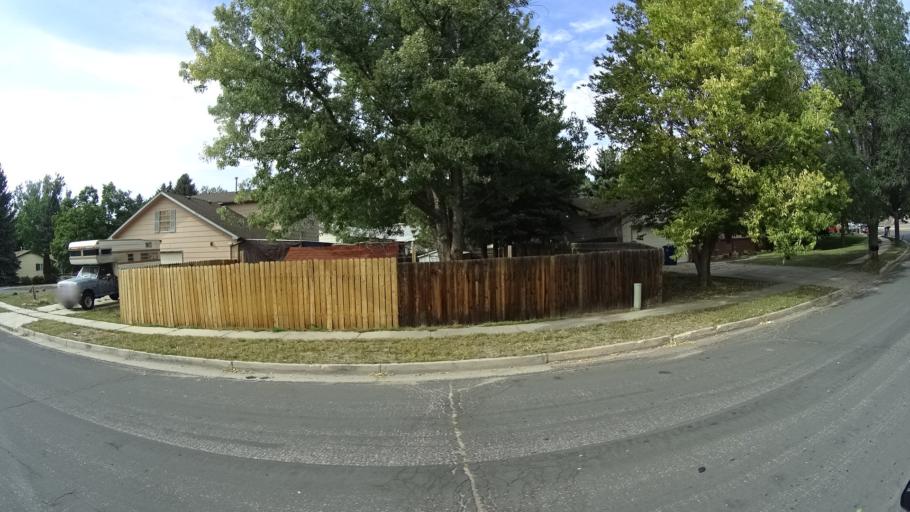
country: US
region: Colorado
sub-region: El Paso County
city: Cimarron Hills
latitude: 38.8949
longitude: -104.7696
